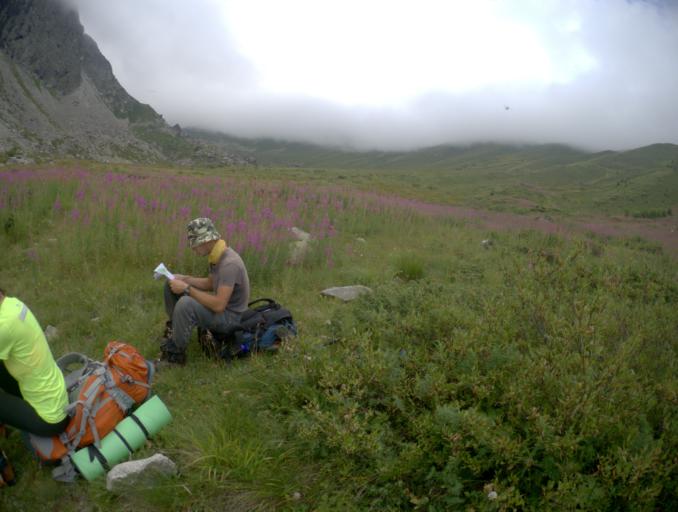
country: RU
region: Karachayevo-Cherkesiya
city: Uchkulan
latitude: 43.3344
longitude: 42.1224
